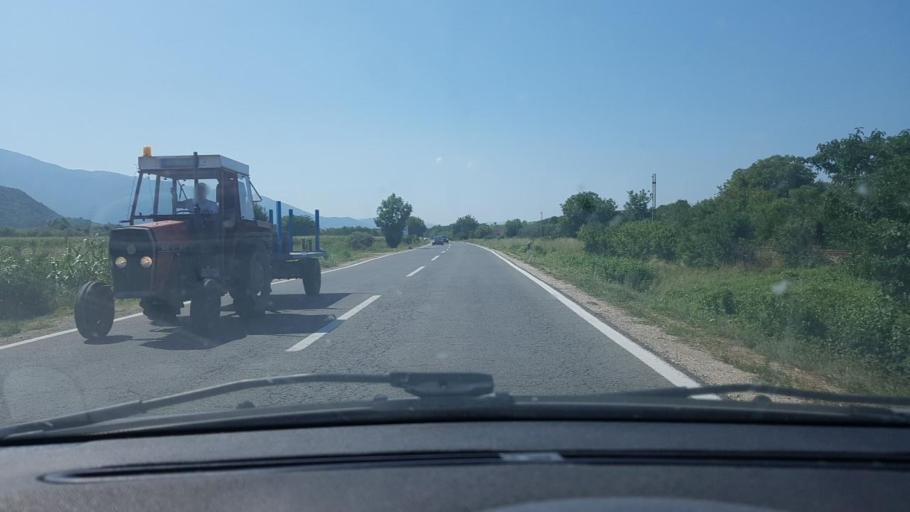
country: BA
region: Federation of Bosnia and Herzegovina
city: Bihac
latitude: 44.8031
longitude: 15.9040
